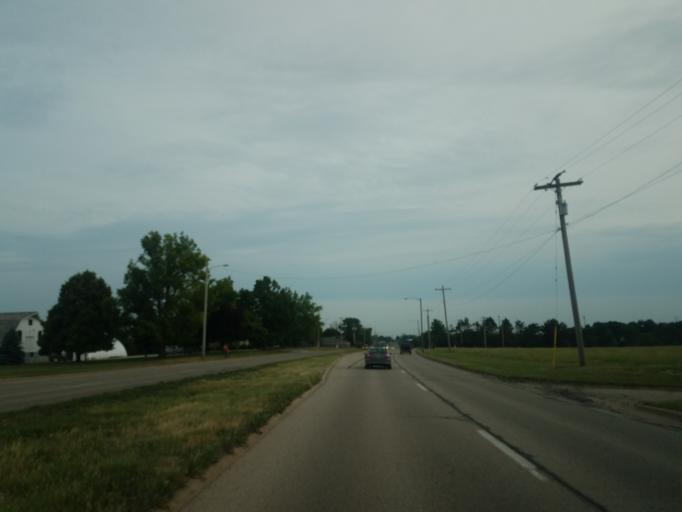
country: US
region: Illinois
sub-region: McLean County
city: Bloomington
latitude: 40.4515
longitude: -88.9924
